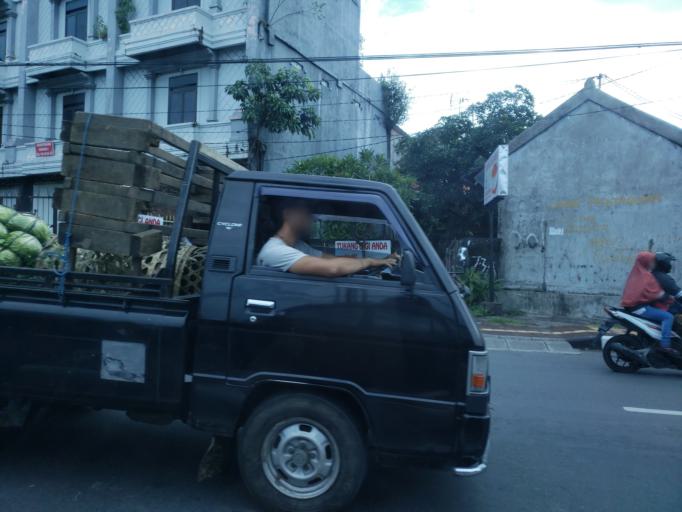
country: ID
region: Bali
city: Denpasar
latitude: -8.6688
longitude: 115.1907
